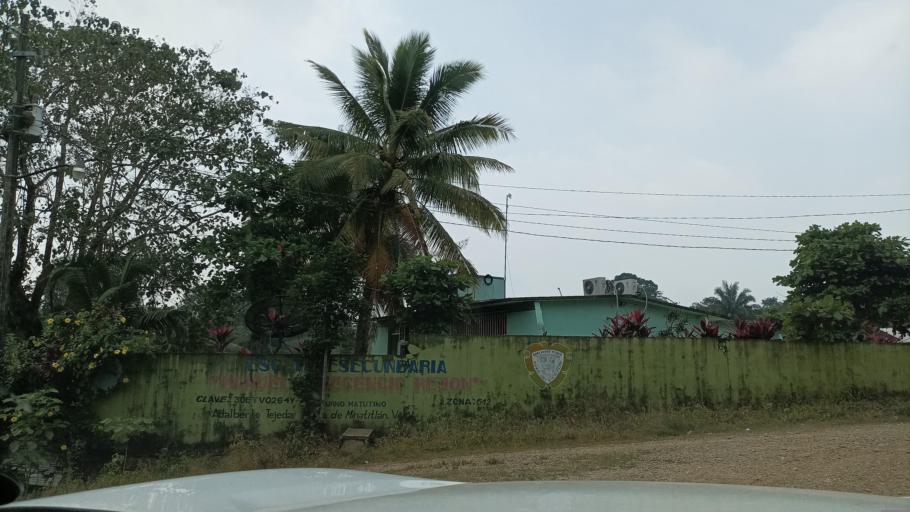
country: MX
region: Veracruz
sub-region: Moloacan
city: Cuichapa
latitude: 17.5780
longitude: -94.2318
